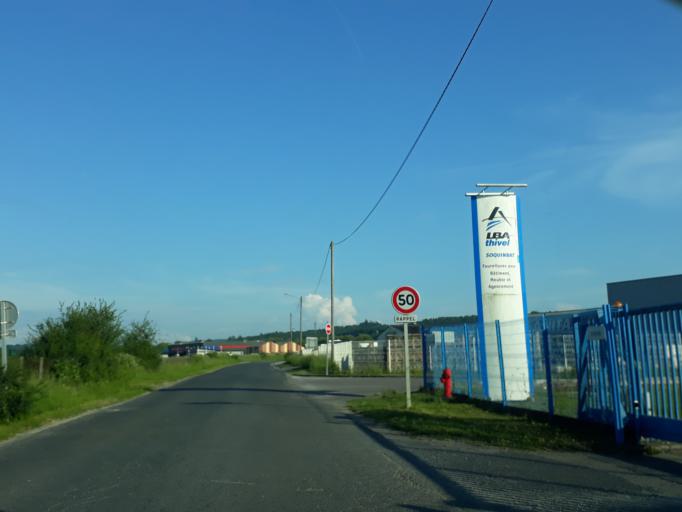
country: FR
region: Limousin
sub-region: Departement de la Correze
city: Saint-Pantaleon-de-Larche
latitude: 45.1514
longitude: 1.4678
